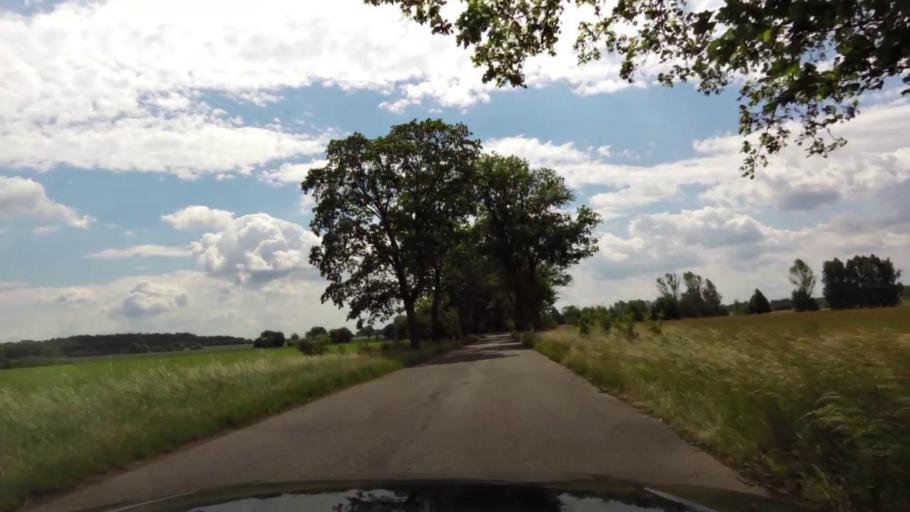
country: PL
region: West Pomeranian Voivodeship
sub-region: Powiat mysliborski
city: Mysliborz
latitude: 52.9680
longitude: 14.8915
